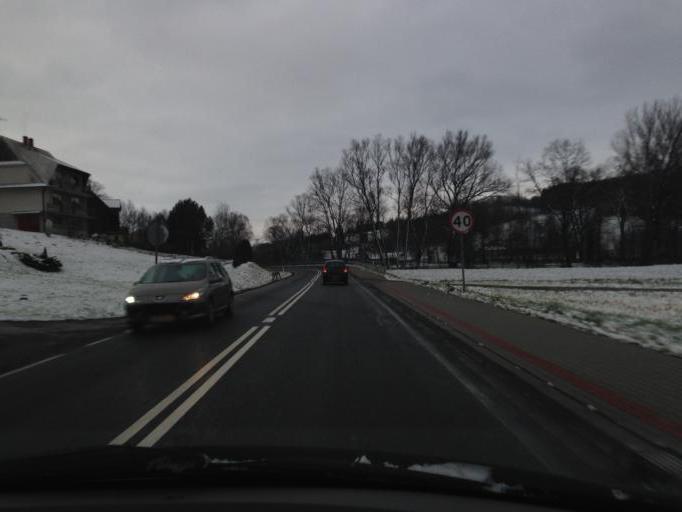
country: PL
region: Lesser Poland Voivodeship
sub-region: Powiat tarnowski
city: Rzepiennik Strzyzewski
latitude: 49.8030
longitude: 21.0389
